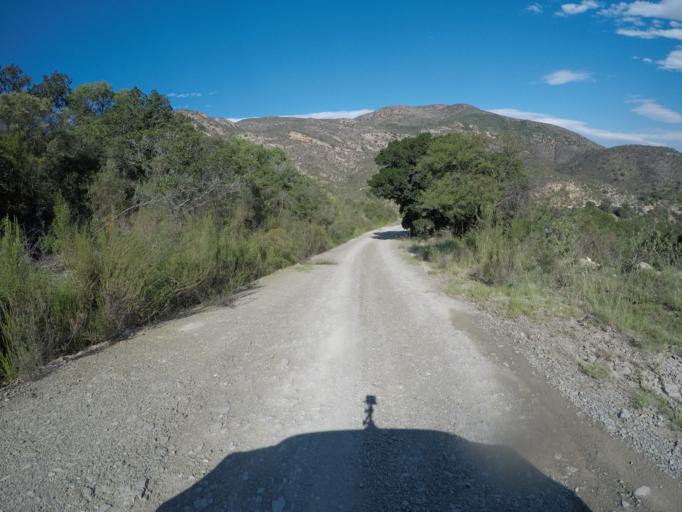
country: ZA
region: Eastern Cape
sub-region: Cacadu District Municipality
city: Kareedouw
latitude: -33.6459
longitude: 24.4564
